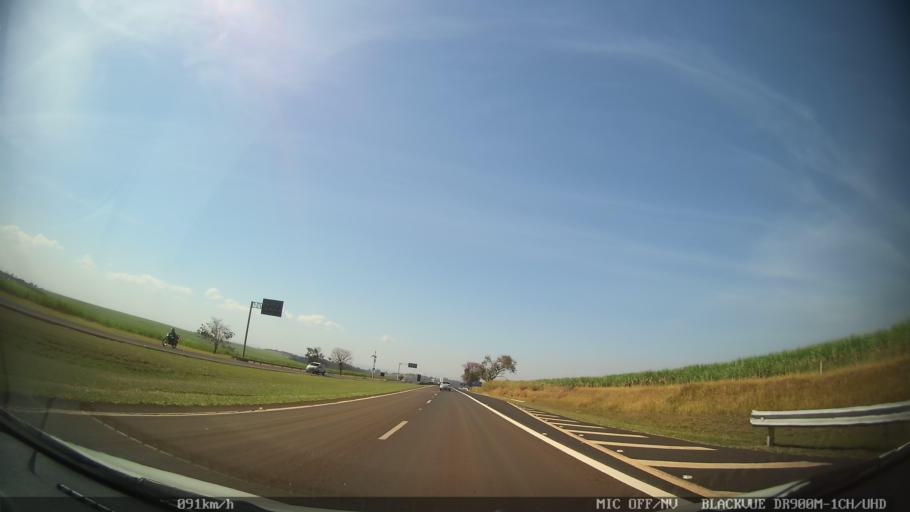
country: BR
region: Sao Paulo
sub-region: Ribeirao Preto
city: Ribeirao Preto
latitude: -21.1665
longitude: -47.8951
